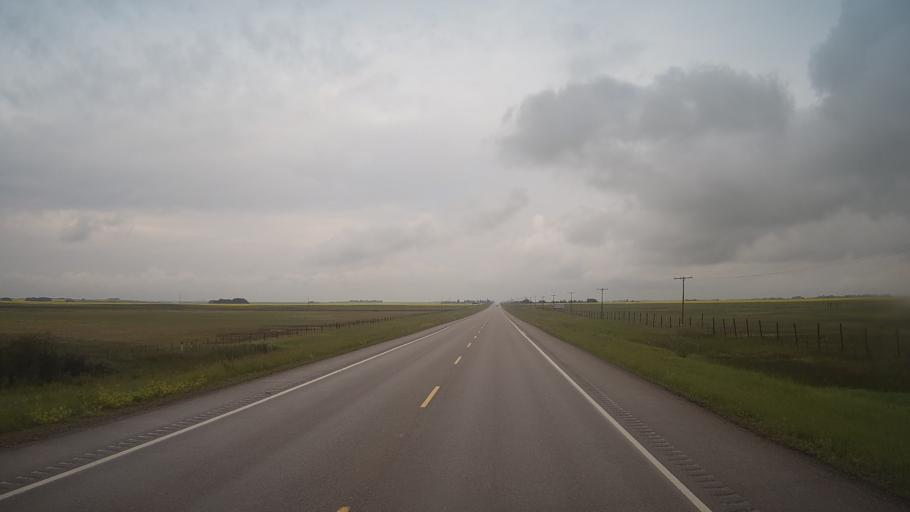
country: CA
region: Saskatchewan
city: Unity
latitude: 52.4349
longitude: -108.9928
